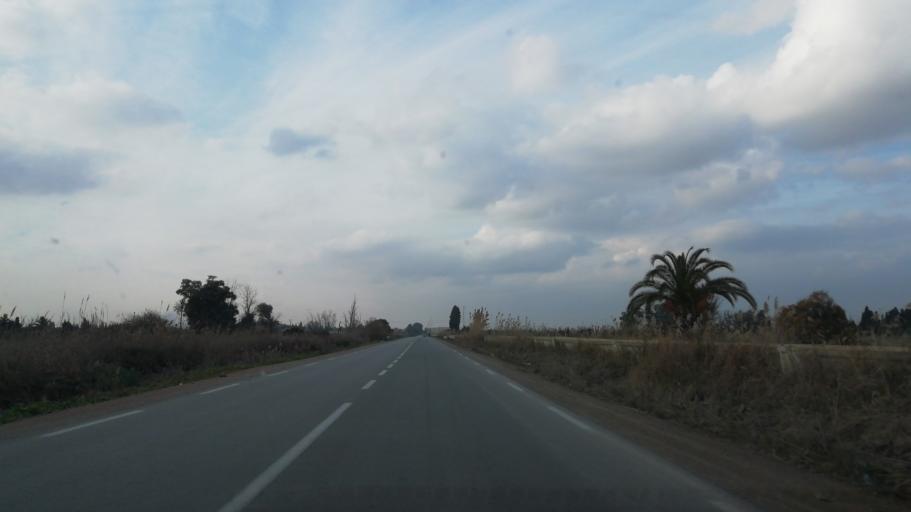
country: DZ
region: Mascara
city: Sig
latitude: 35.6500
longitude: 0.0230
